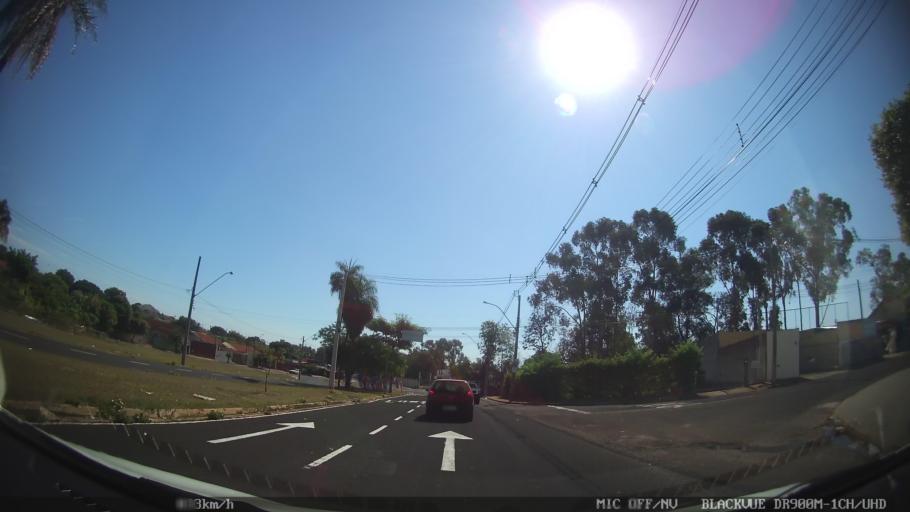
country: BR
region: Sao Paulo
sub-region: Sao Jose Do Rio Preto
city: Sao Jose do Rio Preto
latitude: -20.7716
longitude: -49.4168
